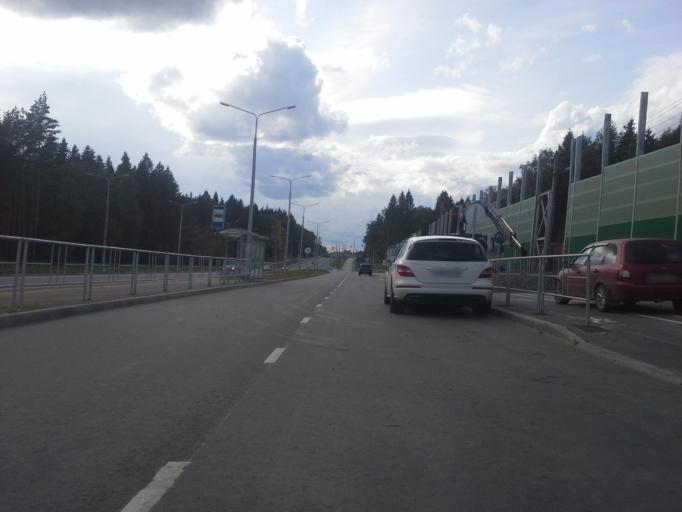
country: RU
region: Moskovskaya
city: Annino
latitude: 55.5336
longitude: 37.2195
